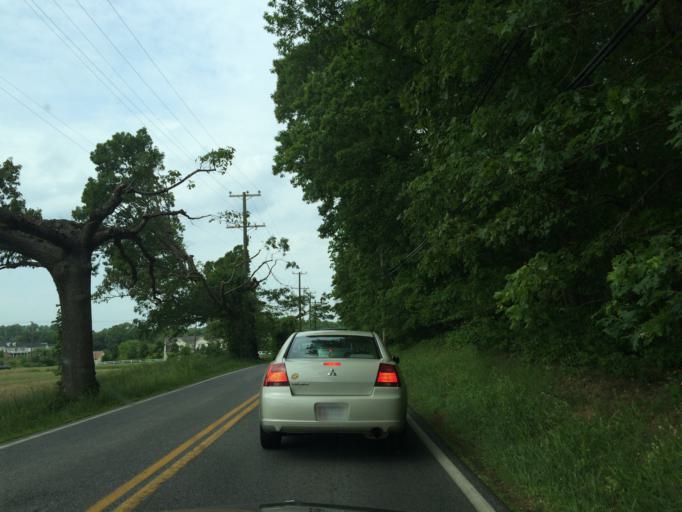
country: US
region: Maryland
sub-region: Howard County
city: Columbia
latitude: 39.2843
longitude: -76.8959
